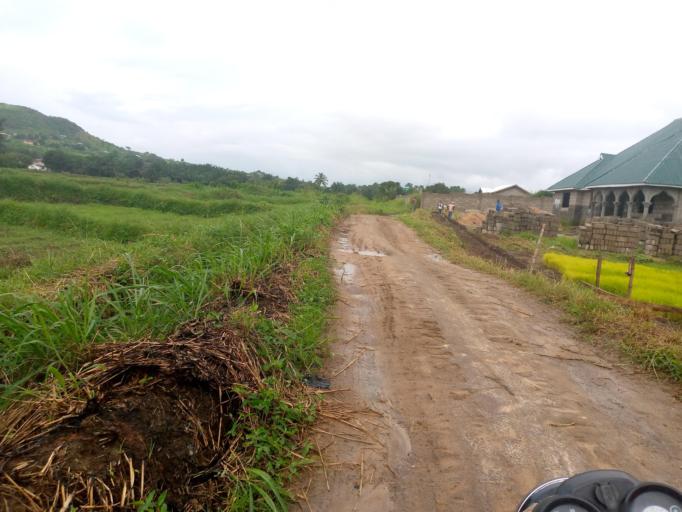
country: SL
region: Eastern Province
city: Kenema
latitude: 7.8520
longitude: -11.2007
